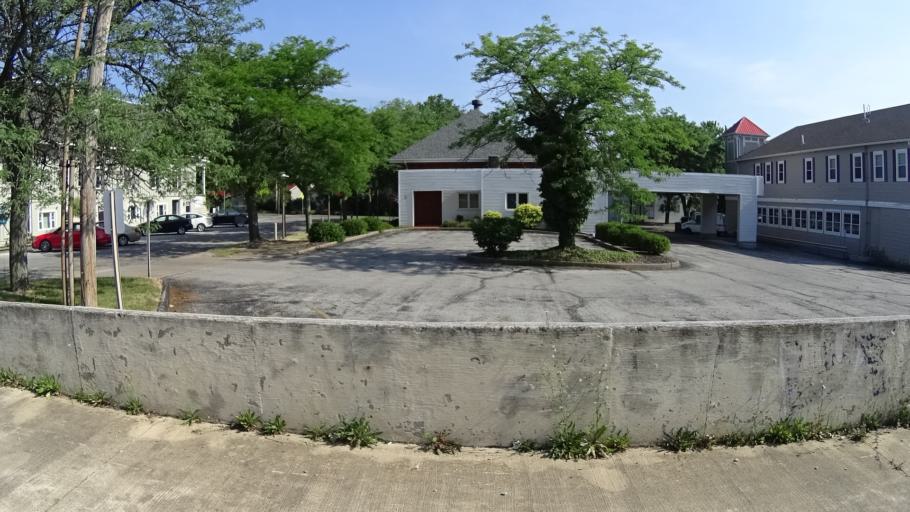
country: US
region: Ohio
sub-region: Lorain County
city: Vermilion
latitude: 41.4214
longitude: -82.3634
